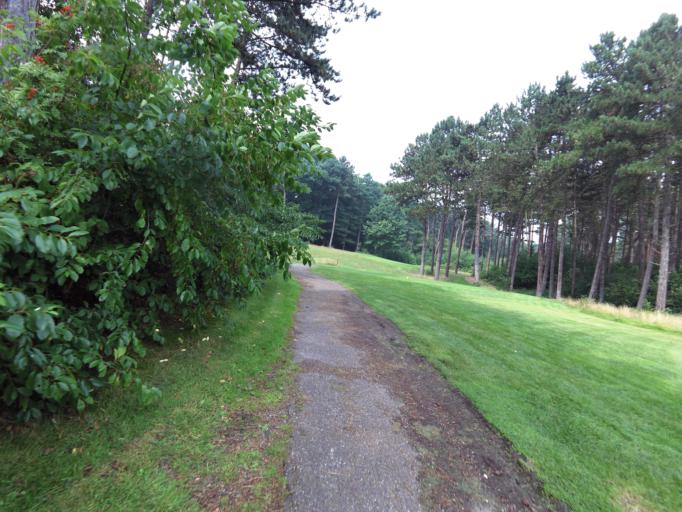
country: NL
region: Limburg
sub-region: Gemeente Brunssum
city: Brunssum
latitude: 50.9357
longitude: 6.0029
